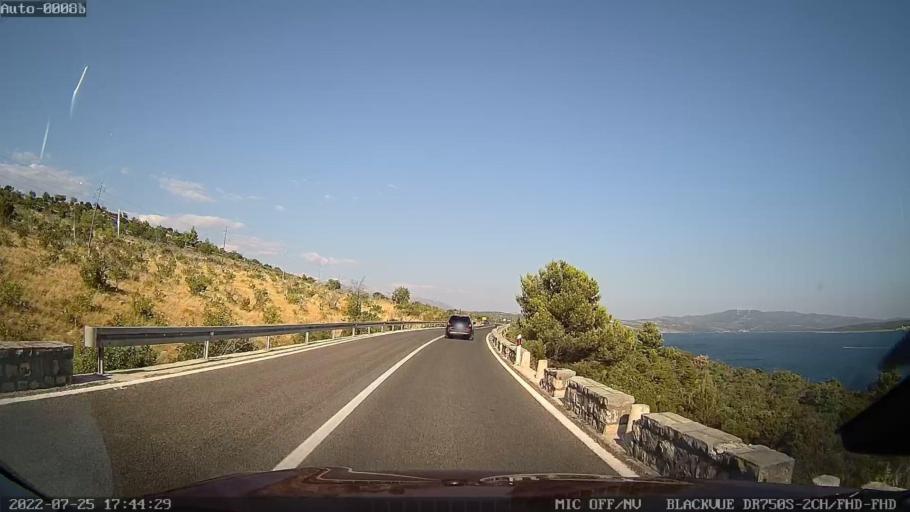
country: HR
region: Zadarska
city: Posedarje
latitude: 44.2224
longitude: 15.5171
